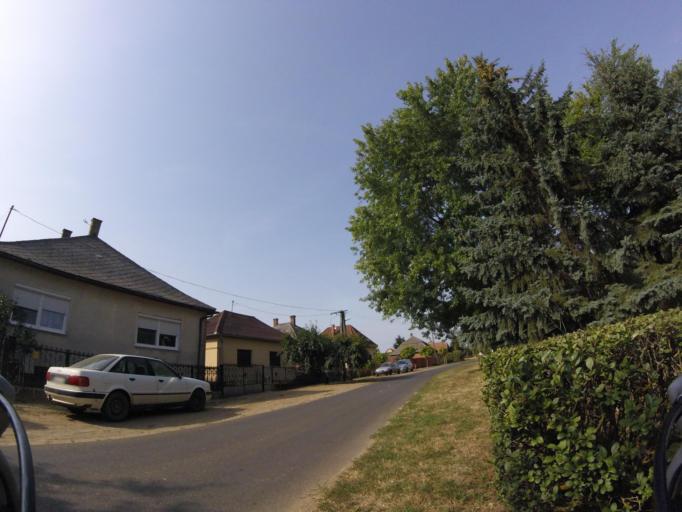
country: HU
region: Szabolcs-Szatmar-Bereg
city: Nyirmada
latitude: 48.1390
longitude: 22.1901
